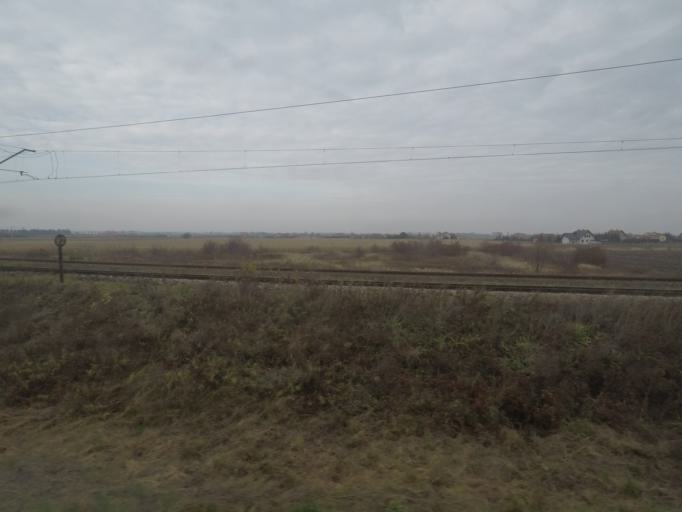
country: PL
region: Subcarpathian Voivodeship
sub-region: Powiat przemyski
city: Zurawica
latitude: 49.7852
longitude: 22.8470
